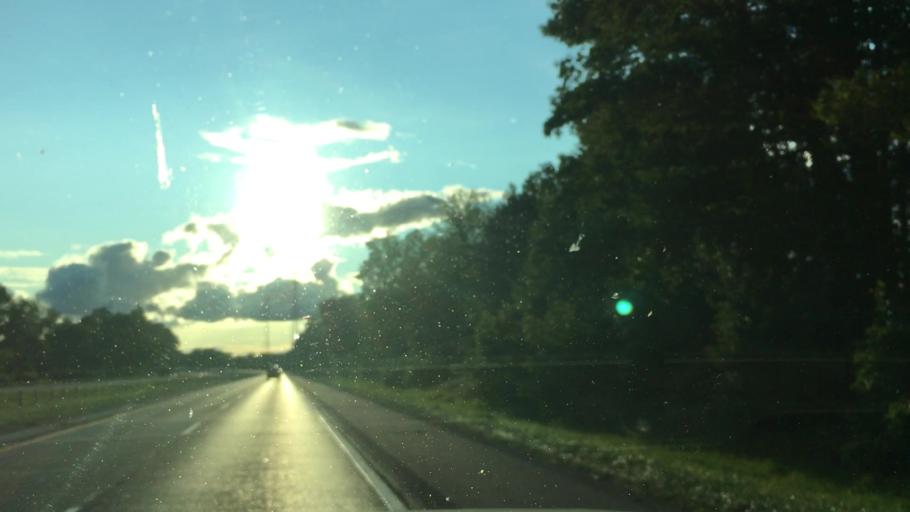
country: US
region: Michigan
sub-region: Kent County
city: Lowell
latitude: 42.8792
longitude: -85.3004
